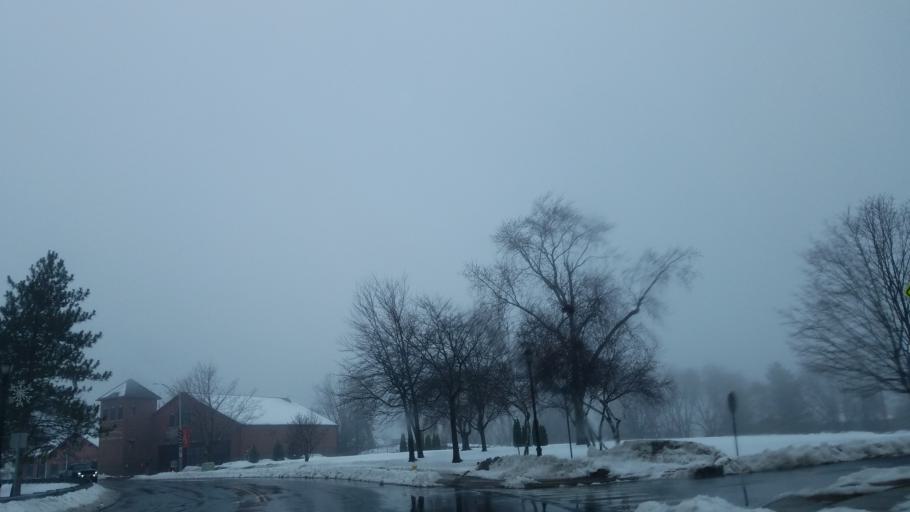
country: US
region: Connecticut
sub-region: Hartford County
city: Thompsonville
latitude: 41.9999
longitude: -72.5963
